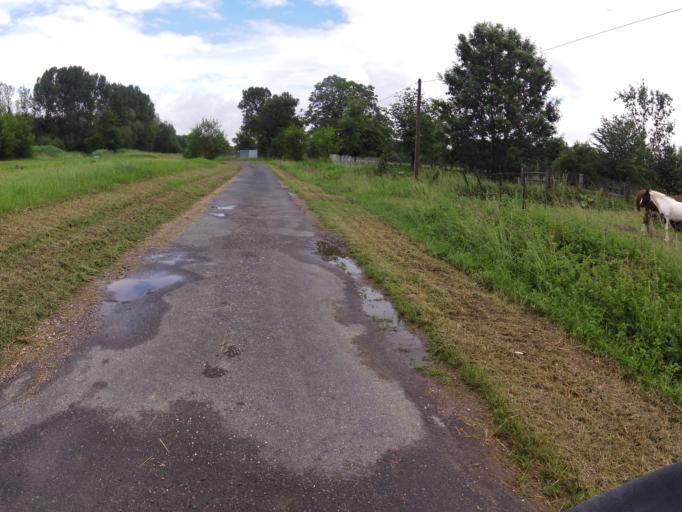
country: FR
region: Champagne-Ardenne
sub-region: Departement de la Marne
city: Sermaize-les-Bains
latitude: 48.7893
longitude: 4.9154
